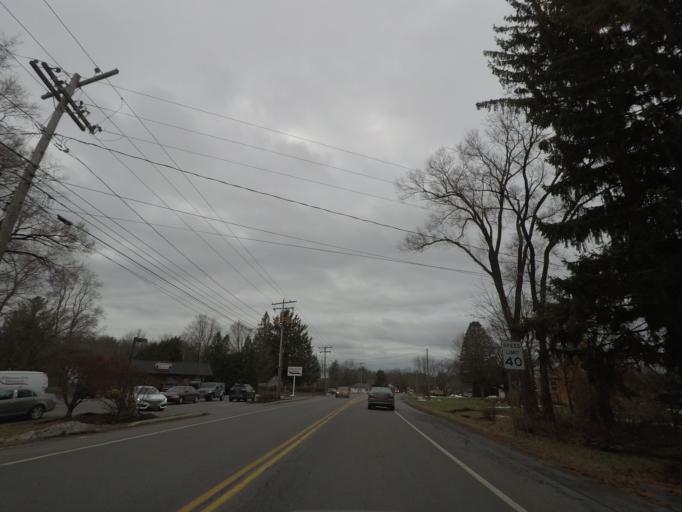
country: US
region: New York
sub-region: Schenectady County
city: East Glenville
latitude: 42.9012
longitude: -73.9058
